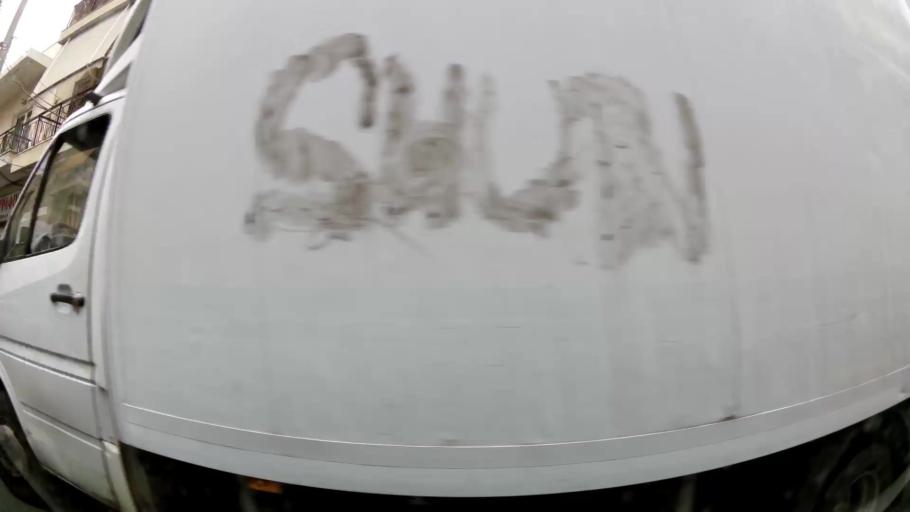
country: GR
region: Attica
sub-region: Nomarchia Athinas
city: Vyronas
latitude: 37.9656
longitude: 23.7560
